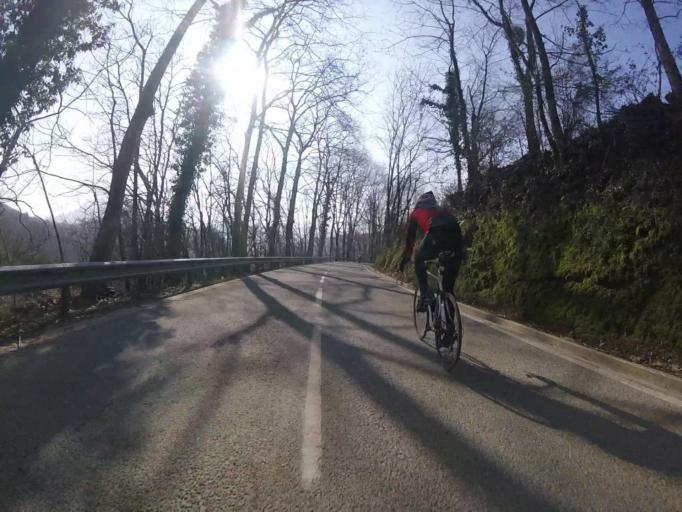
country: ES
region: Navarre
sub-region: Provincia de Navarra
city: Bera
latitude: 43.2981
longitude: -1.6895
